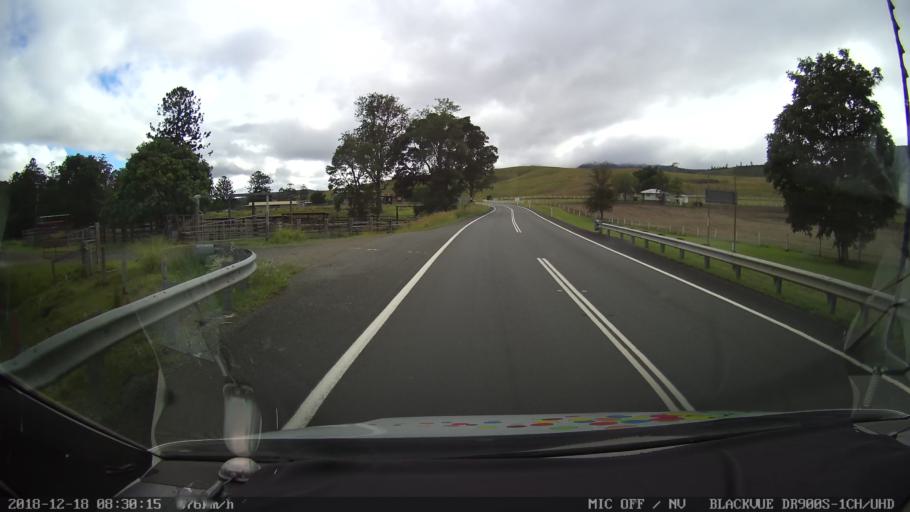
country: AU
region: New South Wales
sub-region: Kyogle
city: Kyogle
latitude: -28.3225
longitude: 152.7672
